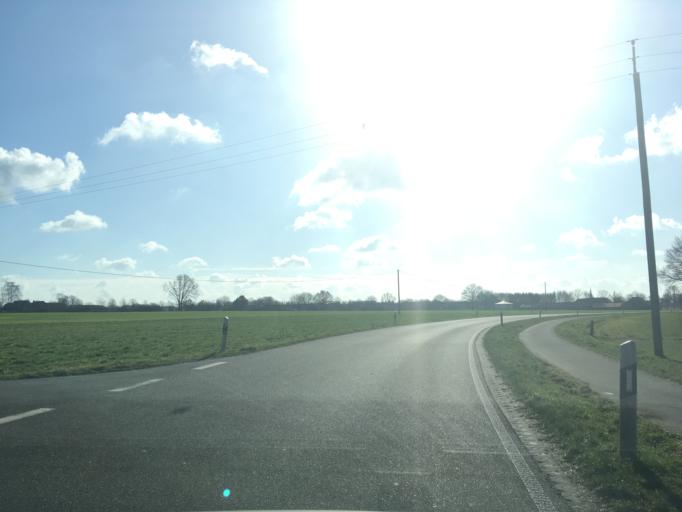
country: DE
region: North Rhine-Westphalia
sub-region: Regierungsbezirk Munster
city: Rhede
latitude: 51.8606
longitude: 6.6936
